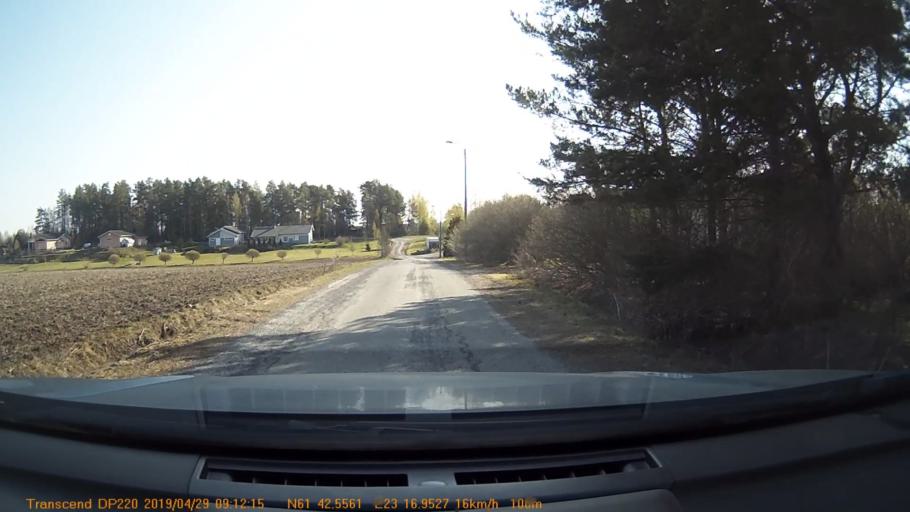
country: FI
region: Pirkanmaa
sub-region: Tampere
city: Viljakkala
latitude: 61.7093
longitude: 23.2827
